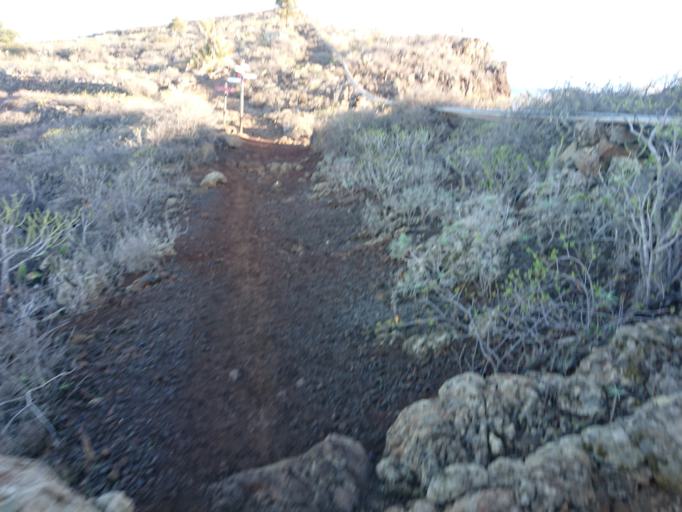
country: ES
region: Canary Islands
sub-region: Provincia de Santa Cruz de Tenerife
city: Los Llanos de Aridane
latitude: 28.6677
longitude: -17.9413
